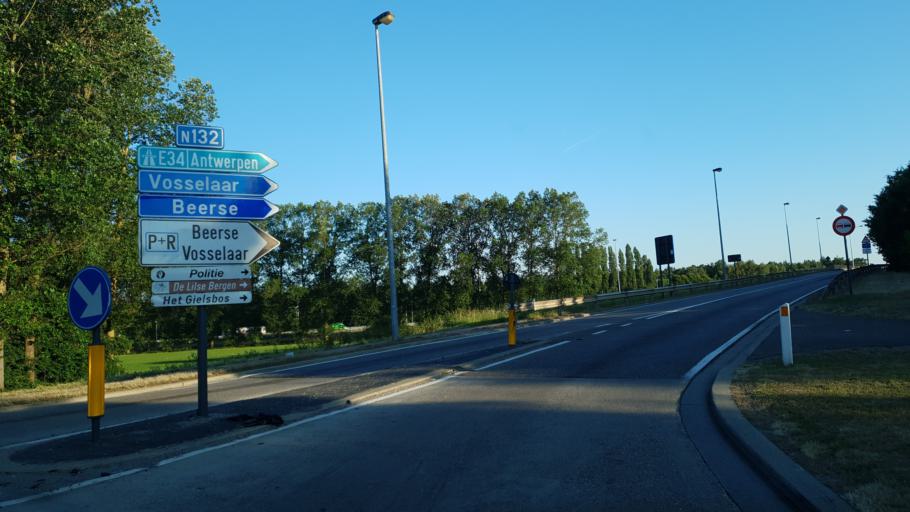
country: BE
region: Flanders
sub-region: Provincie Antwerpen
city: Beerse
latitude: 51.2843
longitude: 4.8568
